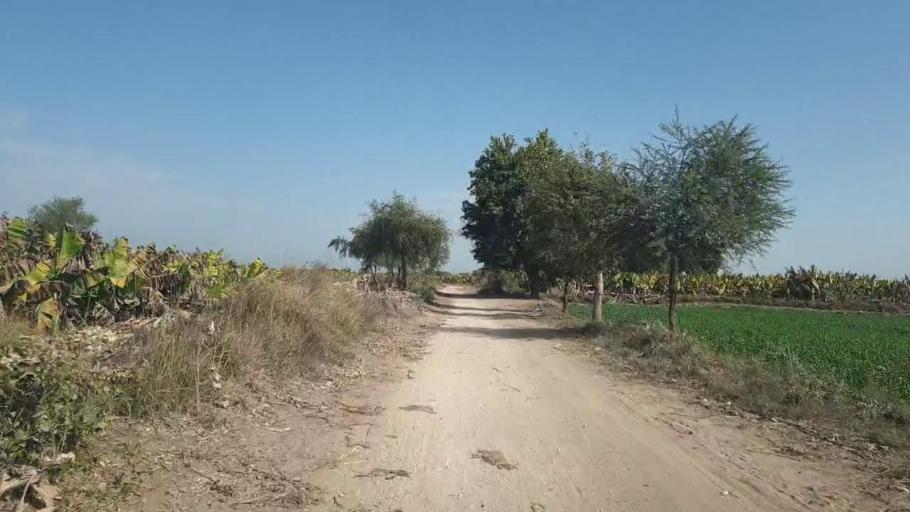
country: PK
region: Sindh
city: Sakrand
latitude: 25.9836
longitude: 68.3463
